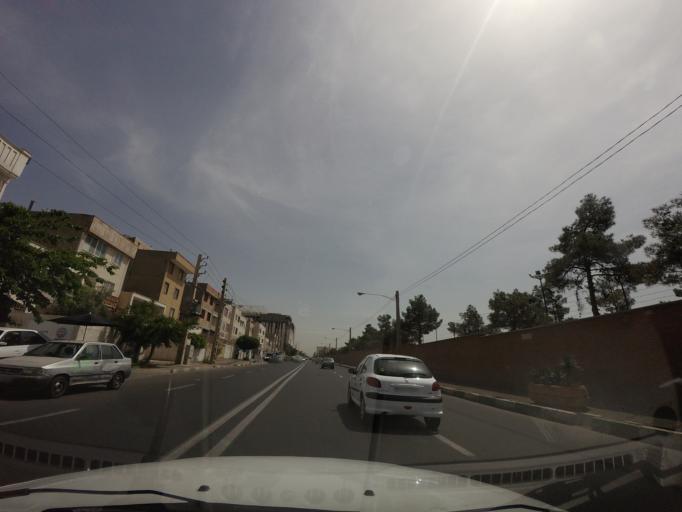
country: IR
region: Tehran
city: Shahr-e Qods
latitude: 35.7448
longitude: 51.2375
